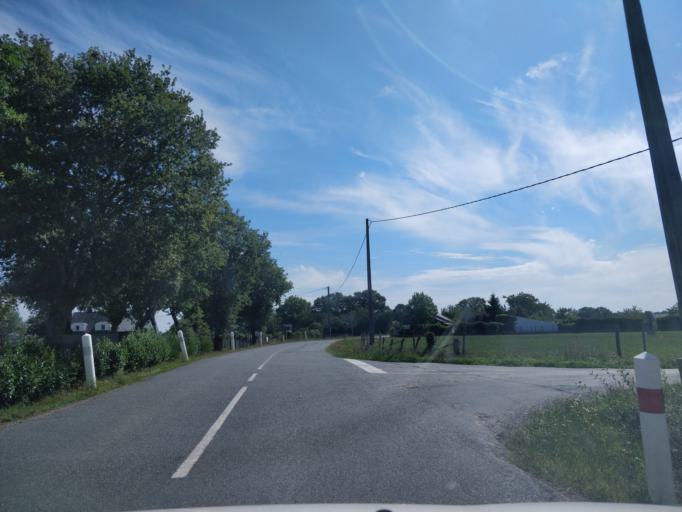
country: FR
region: Brittany
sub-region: Departement d'Ille-et-Vilaine
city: Grand-Fougeray
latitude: 47.6890
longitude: -1.7086
